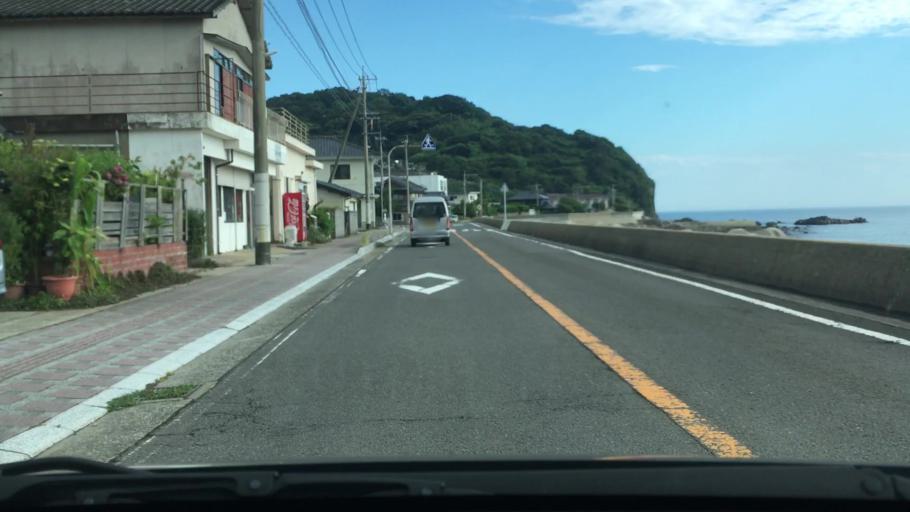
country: JP
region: Nagasaki
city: Togitsu
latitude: 32.8318
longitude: 129.7189
